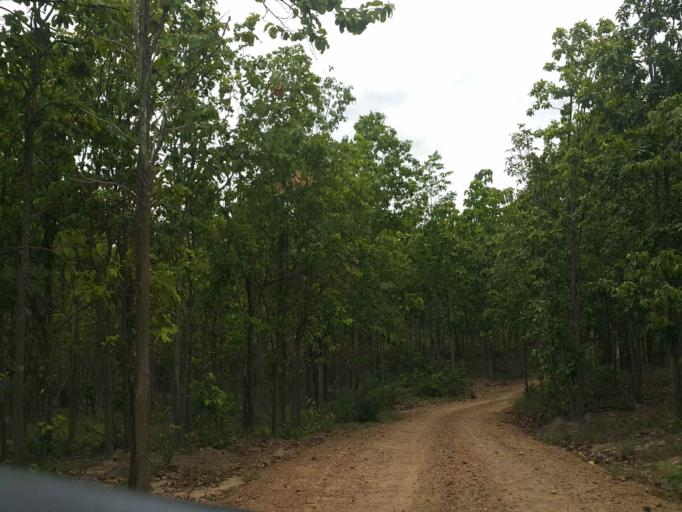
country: TH
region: Chiang Mai
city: Doi Lo
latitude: 18.5000
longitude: 98.7418
